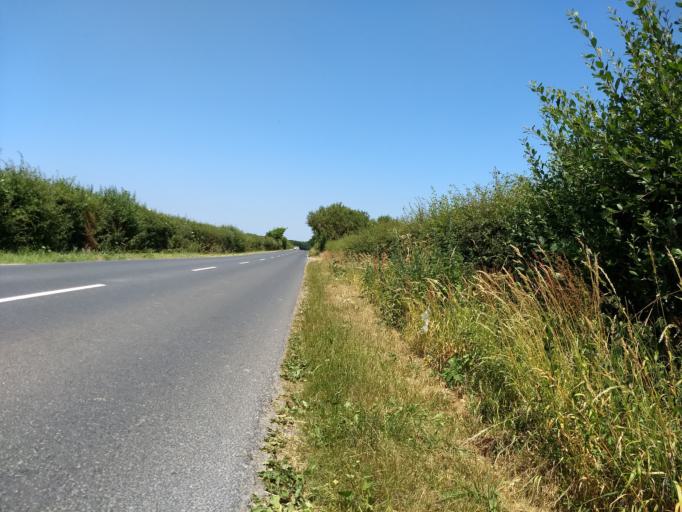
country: GB
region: England
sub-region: Isle of Wight
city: Northwood
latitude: 50.7048
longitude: -1.3465
